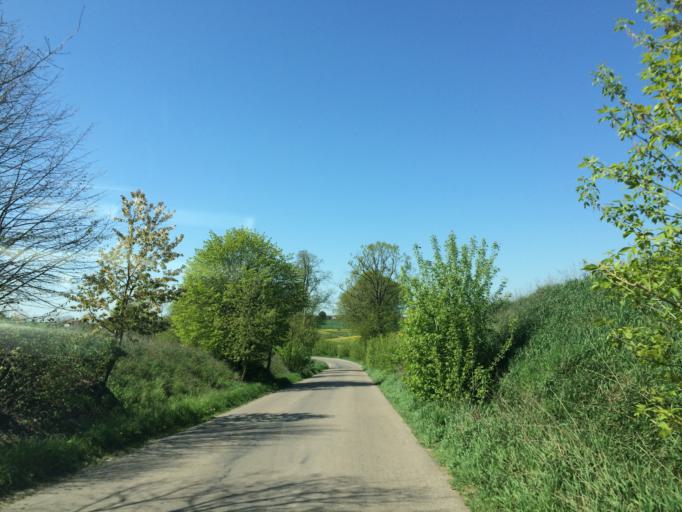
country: PL
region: Warmian-Masurian Voivodeship
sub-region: Powiat nowomiejski
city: Biskupiec
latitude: 53.4687
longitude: 19.2672
